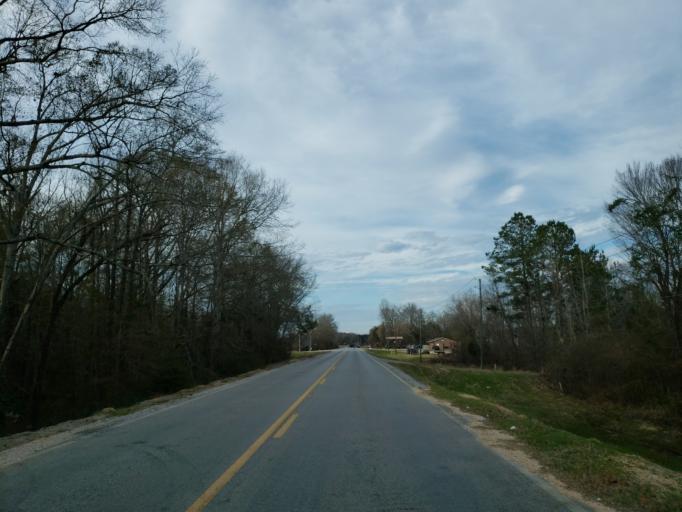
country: US
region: Mississippi
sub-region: Clarke County
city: Quitman
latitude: 31.8637
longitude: -88.7008
